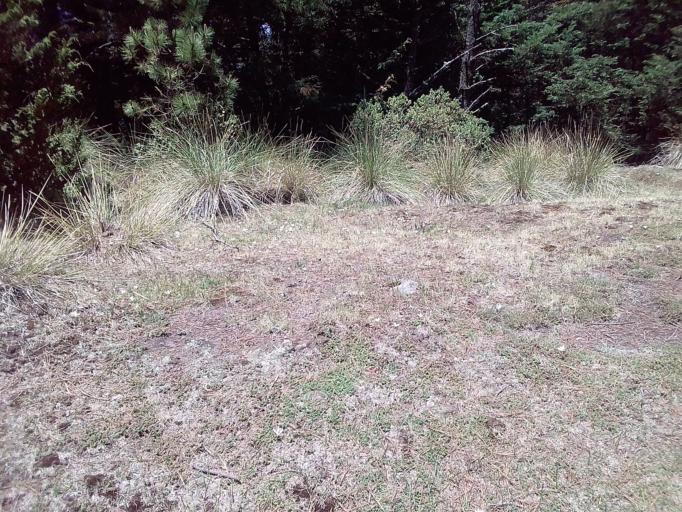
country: MX
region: Mexico City
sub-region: Cuajimalpa de Morelos
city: San Lorenzo Acopilco
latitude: 19.2867
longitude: -99.3346
